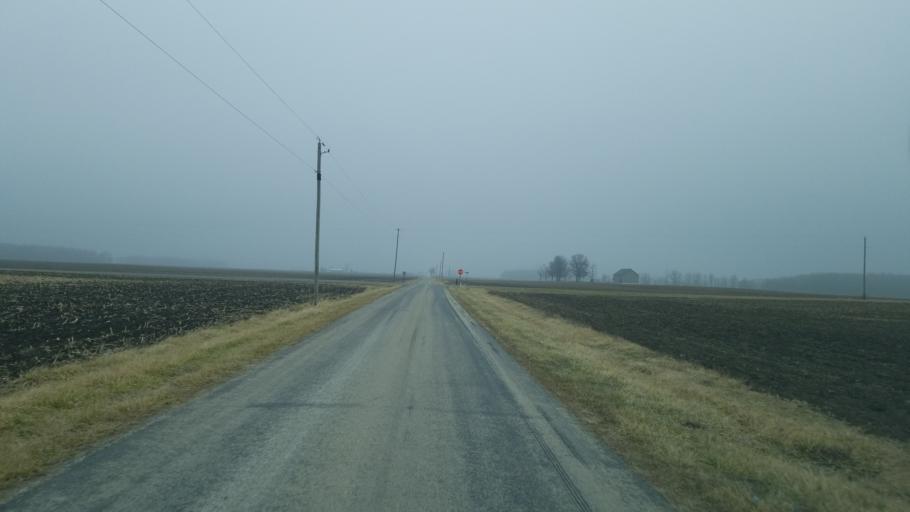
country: US
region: Indiana
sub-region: Wells County
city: Bluffton
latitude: 40.6099
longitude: -85.1071
